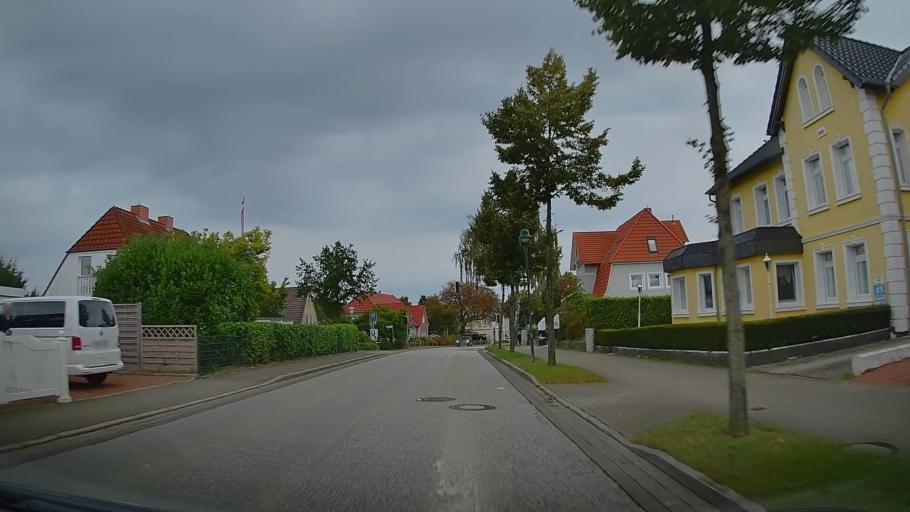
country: DE
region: Schleswig-Holstein
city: Heikendorf
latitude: 54.3661
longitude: 10.2032
